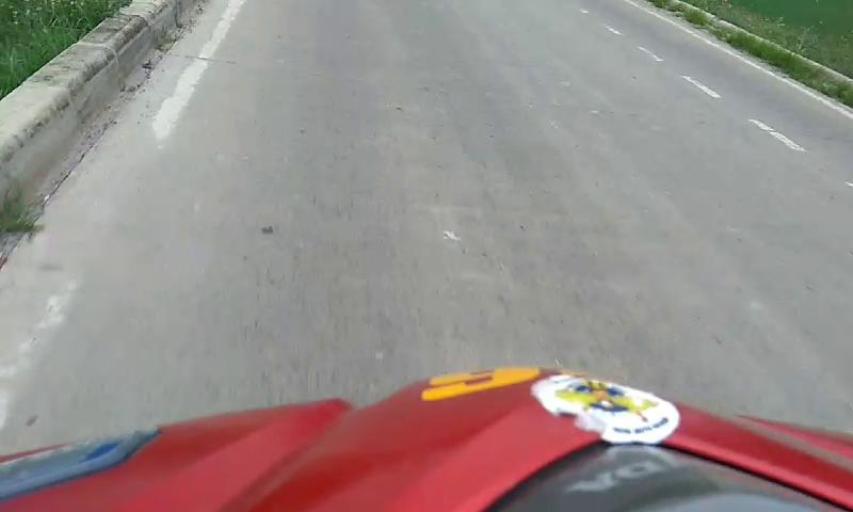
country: ID
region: West Java
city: Bekasi
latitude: -6.1449
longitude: 106.9702
